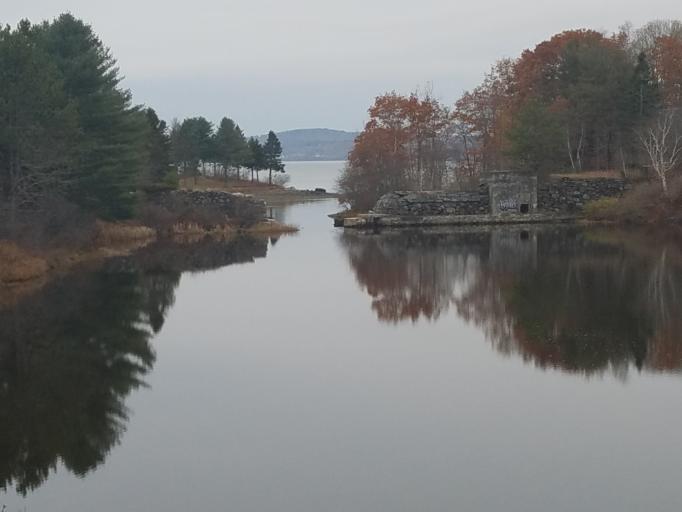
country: US
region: Maine
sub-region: Waldo County
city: Belfast
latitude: 44.4327
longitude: -68.9936
